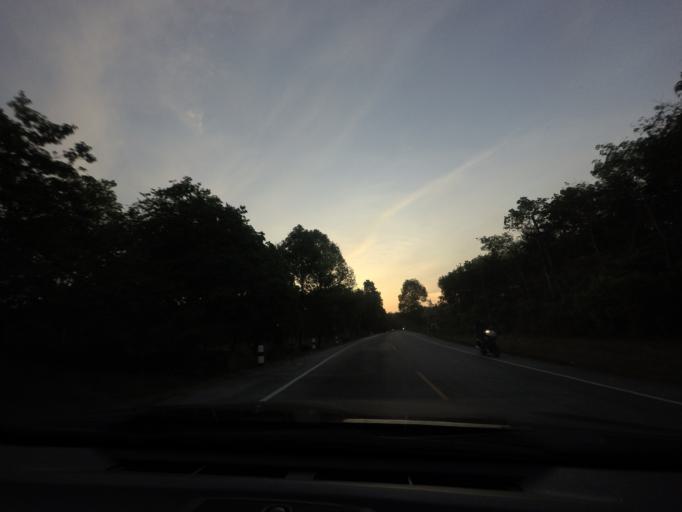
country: TH
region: Narathiwat
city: Rueso
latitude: 6.3556
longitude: 101.5638
